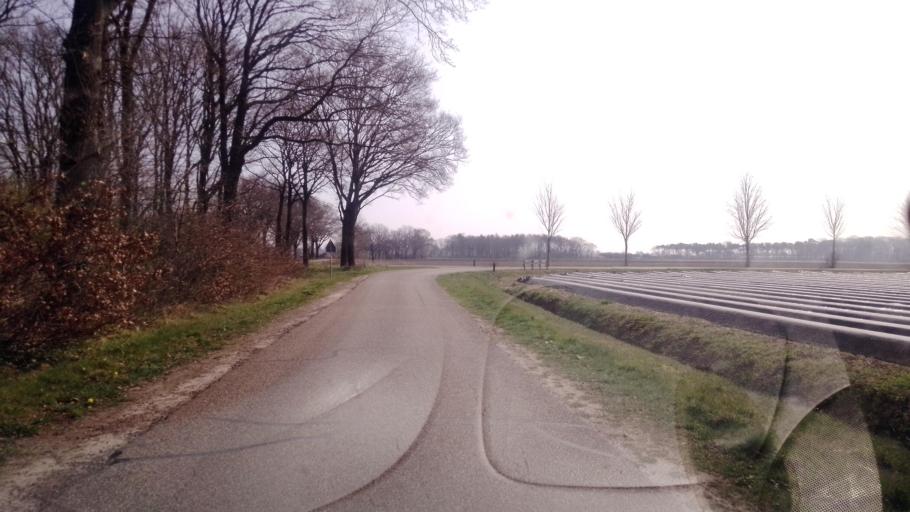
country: NL
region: Limburg
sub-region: Gemeente Peel en Maas
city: Maasbree
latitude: 51.3777
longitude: 6.0330
